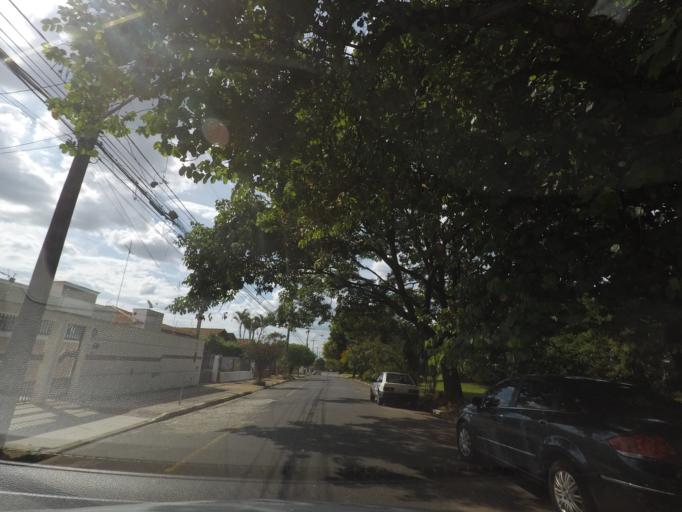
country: BR
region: Sao Paulo
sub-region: Campinas
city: Campinas
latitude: -22.8888
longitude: -47.1036
